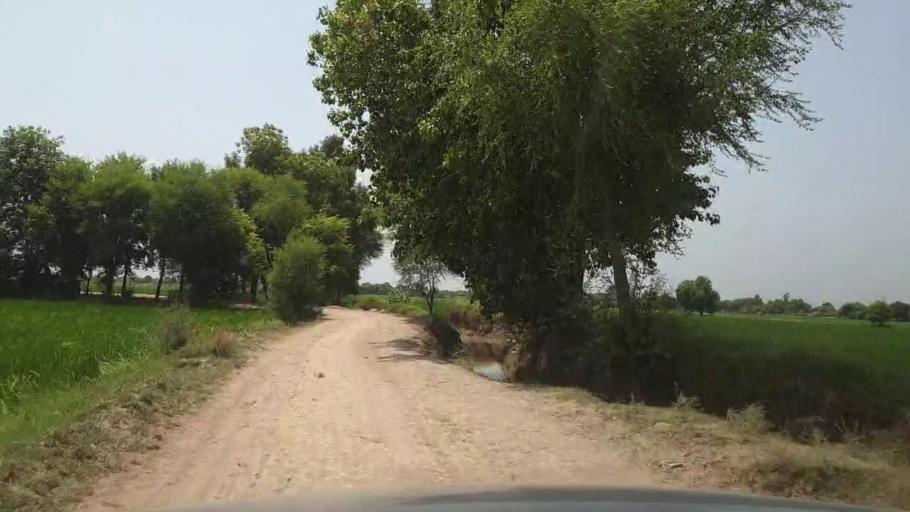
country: PK
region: Sindh
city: Ratodero
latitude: 27.7897
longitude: 68.3475
